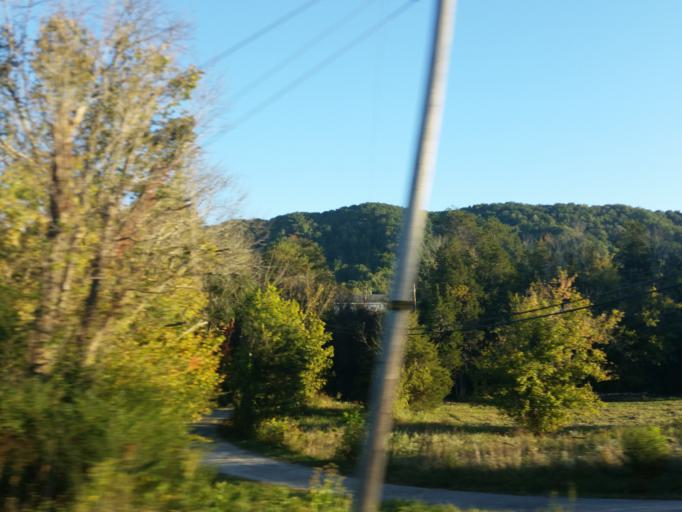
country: US
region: Tennessee
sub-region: Grainger County
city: Rutledge
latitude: 36.3100
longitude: -83.5535
